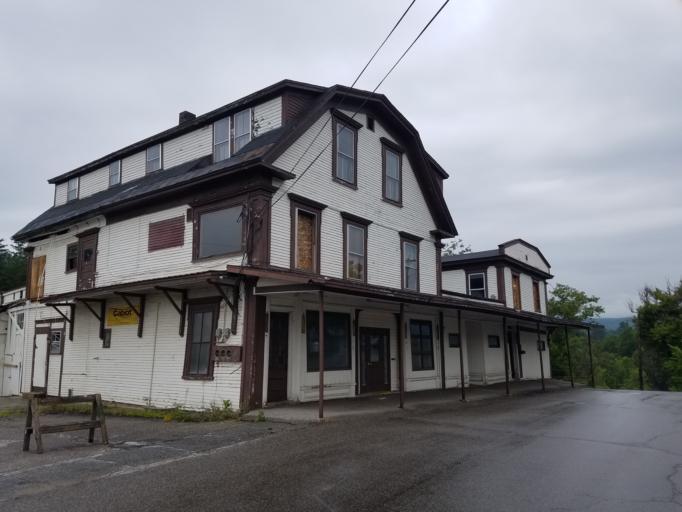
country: US
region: New Hampshire
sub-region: Coos County
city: Whitefield
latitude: 44.3737
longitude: -71.6137
